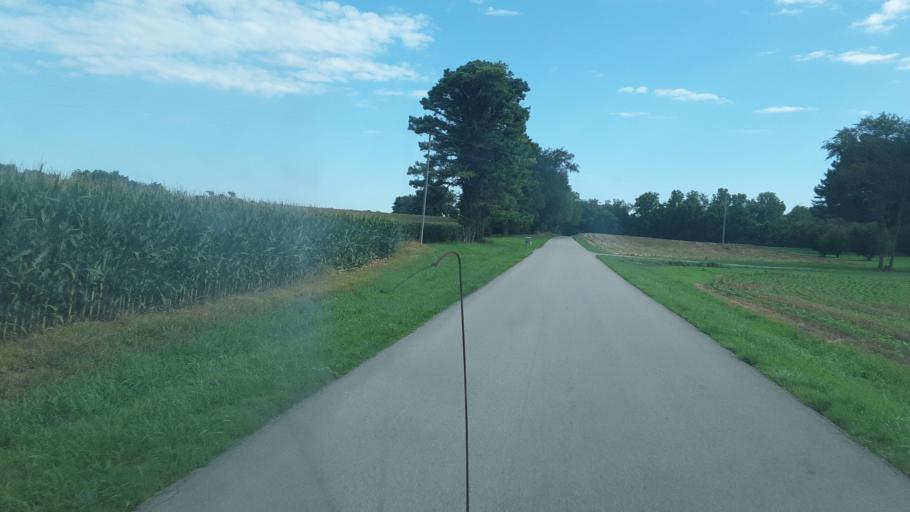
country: US
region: Kentucky
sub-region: Todd County
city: Guthrie
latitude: 36.6724
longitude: -87.1694
